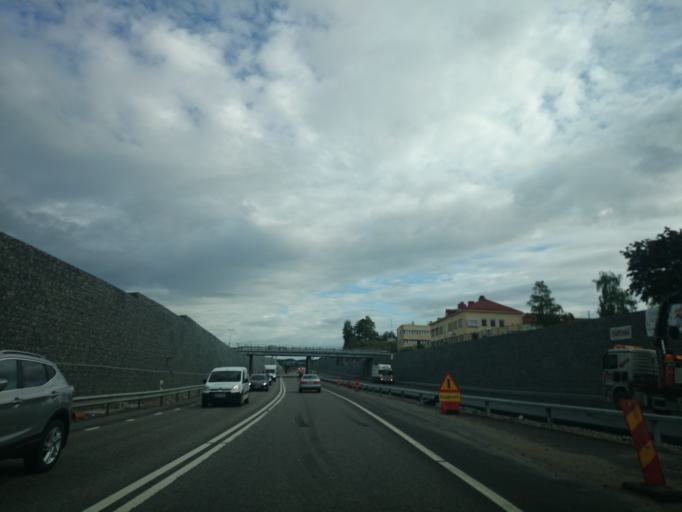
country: SE
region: Vaesternorrland
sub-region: Sundsvalls Kommun
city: Sundsvall
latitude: 62.3995
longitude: 17.3369
